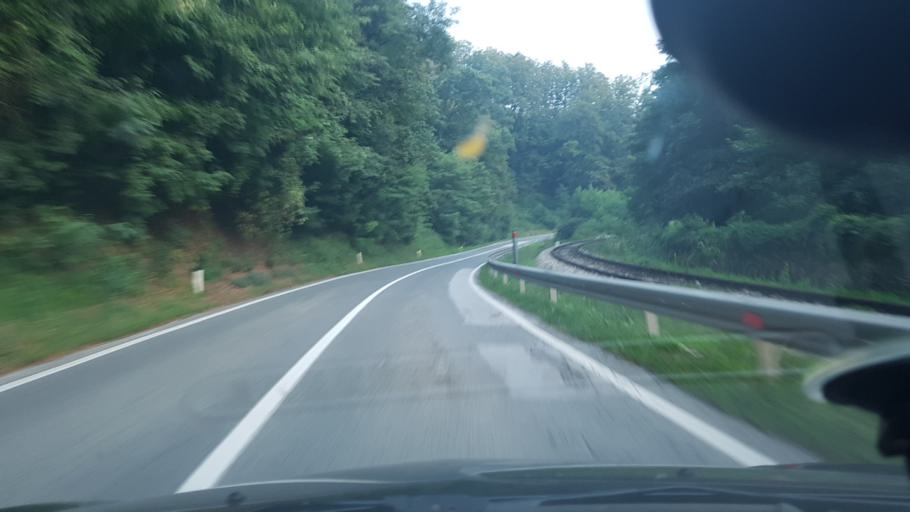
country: SI
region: Rogatec
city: Rogatec
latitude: 46.2222
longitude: 15.7293
